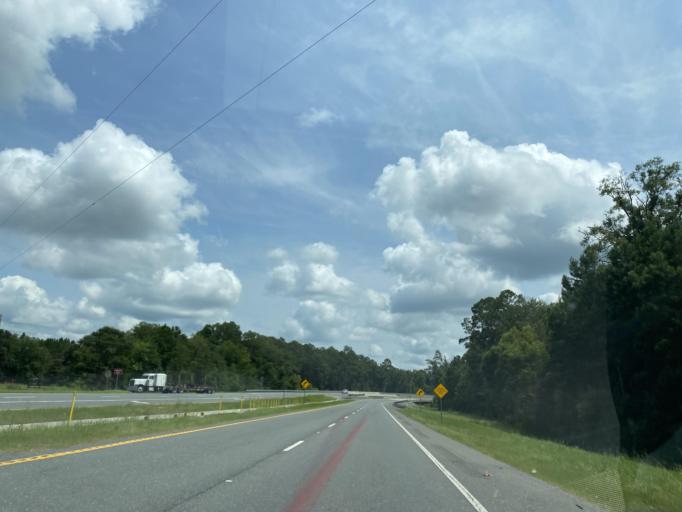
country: US
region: Georgia
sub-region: Ware County
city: Deenwood
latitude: 31.3212
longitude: -82.4589
